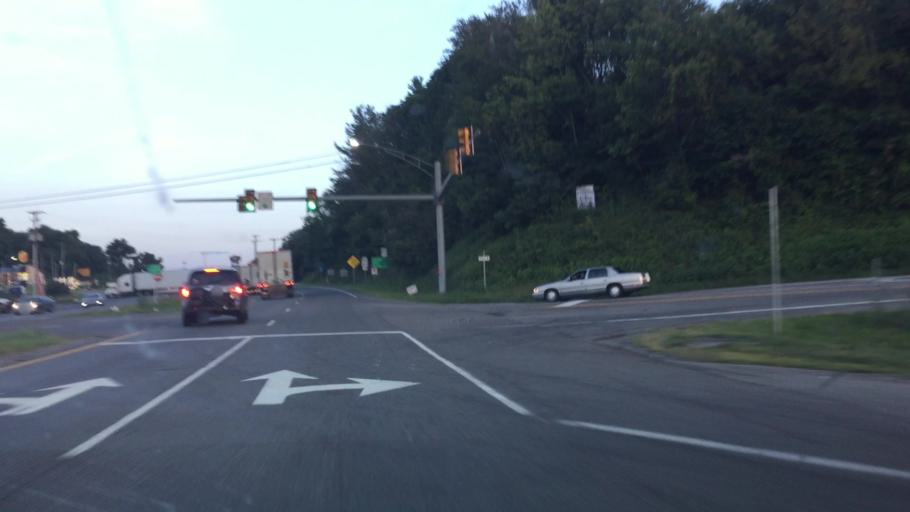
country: US
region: Virginia
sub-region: Wythe County
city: Wytheville
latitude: 36.9451
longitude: -80.9484
